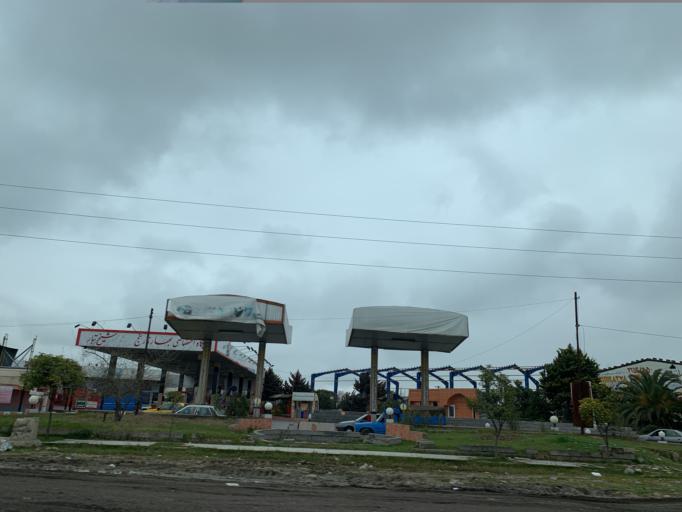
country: IR
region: Mazandaran
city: Babol
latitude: 36.5220
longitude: 52.6013
